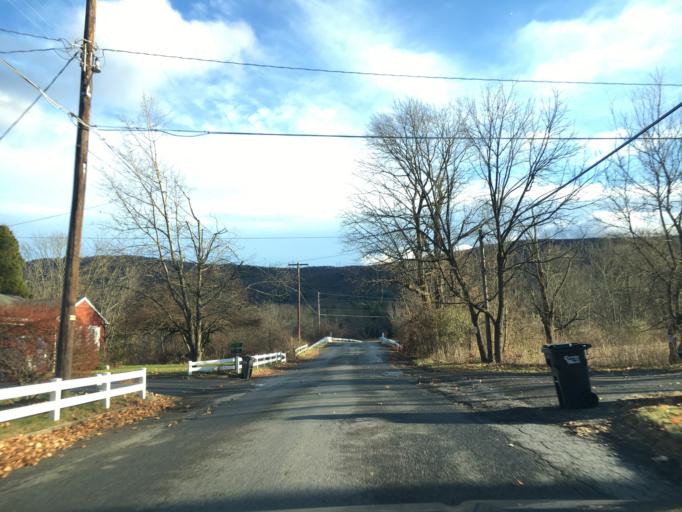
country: US
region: Pennsylvania
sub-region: Carbon County
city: Lehighton
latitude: 40.7829
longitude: -75.7116
